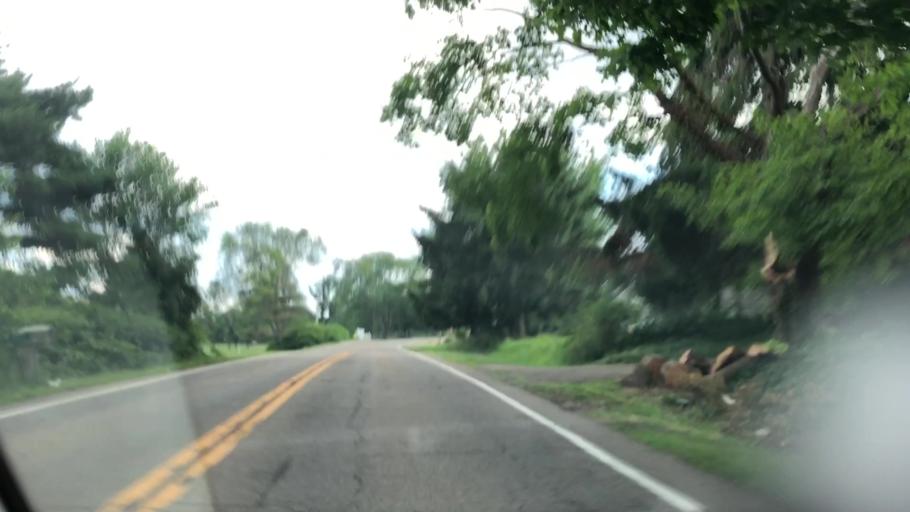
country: US
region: Ohio
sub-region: Summit County
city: Norton
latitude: 41.0632
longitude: -81.6379
